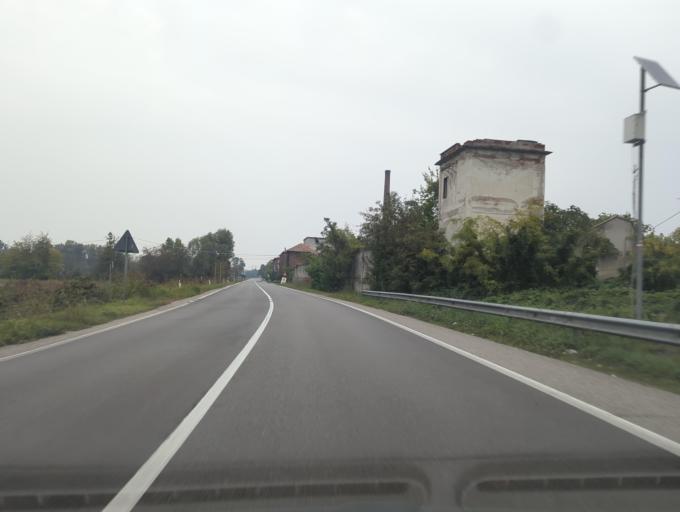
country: IT
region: Lombardy
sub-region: Citta metropolitana di Milano
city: Turbigo
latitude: 45.5161
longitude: 8.7263
